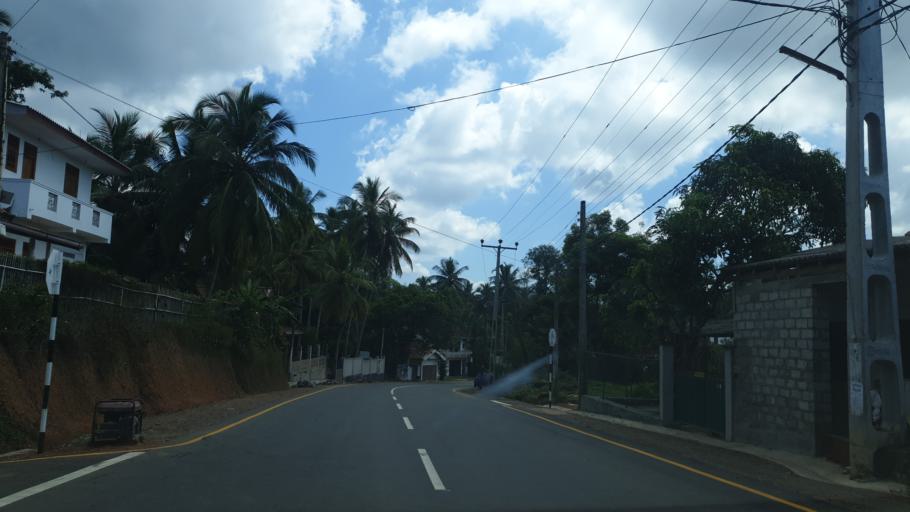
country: LK
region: Western
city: Panadura
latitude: 6.6677
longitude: 79.9476
